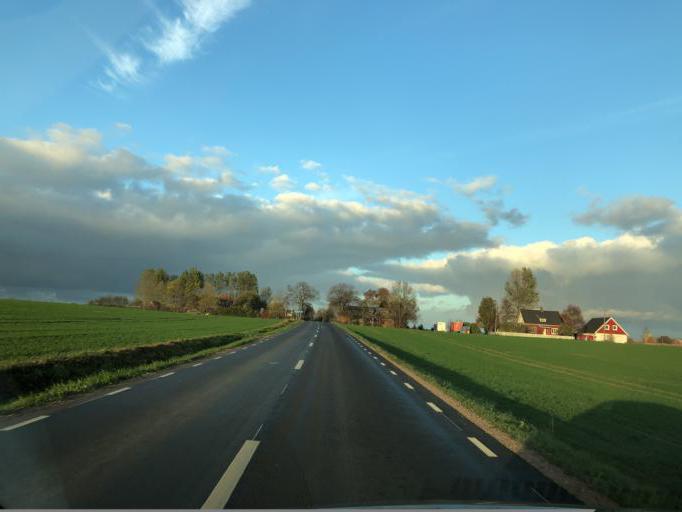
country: SE
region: Skane
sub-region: Svalovs Kommun
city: Svaloev
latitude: 55.8952
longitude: 13.1844
